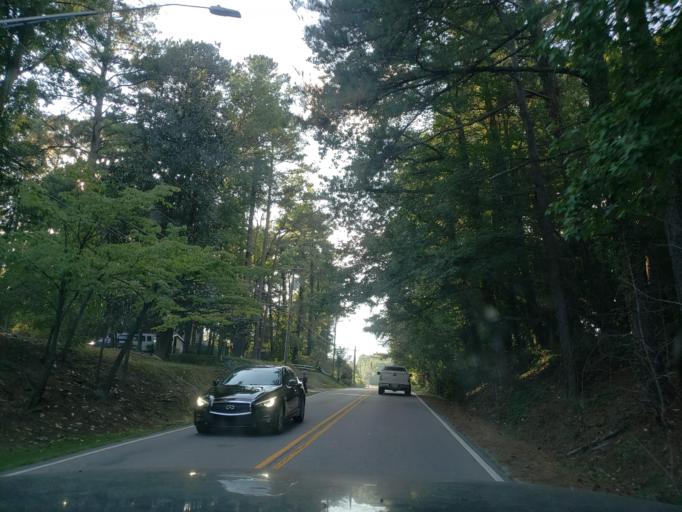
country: US
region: North Carolina
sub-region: Durham County
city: Durham
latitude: 35.9719
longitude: -78.9305
